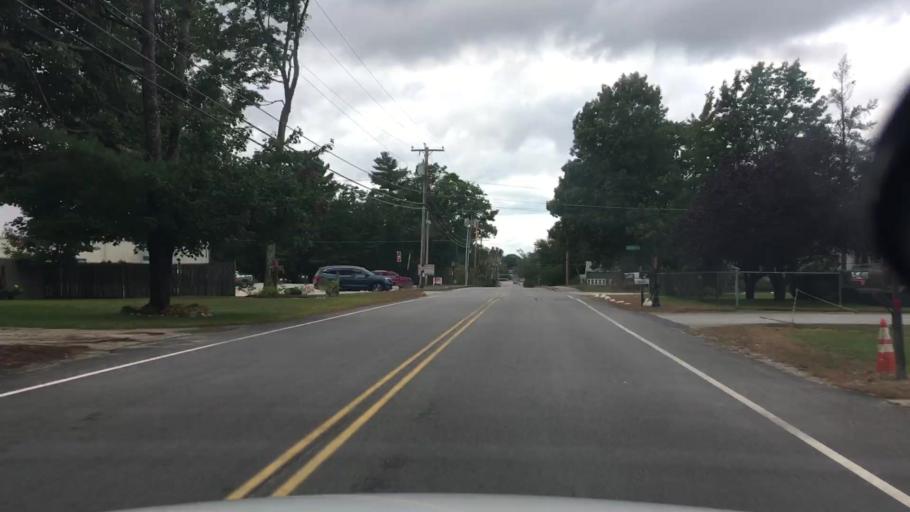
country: US
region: New Hampshire
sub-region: Strafford County
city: Rochester
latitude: 43.2908
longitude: -70.9684
